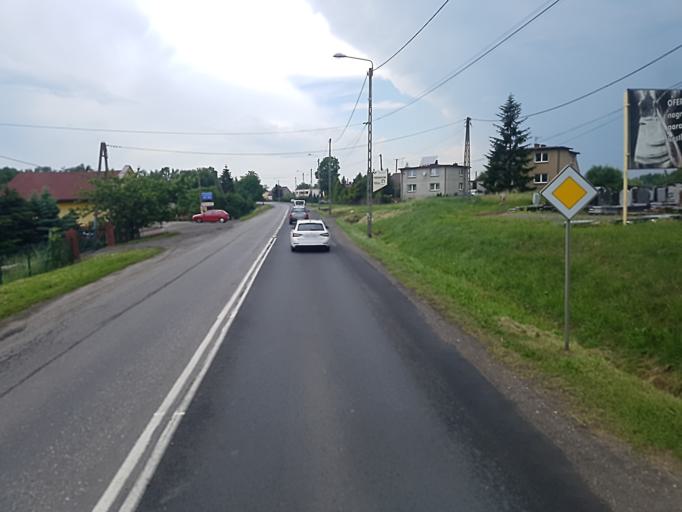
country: PL
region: Silesian Voivodeship
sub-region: Powiat wodzislawski
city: Mszana
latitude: 49.9747
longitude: 18.5317
